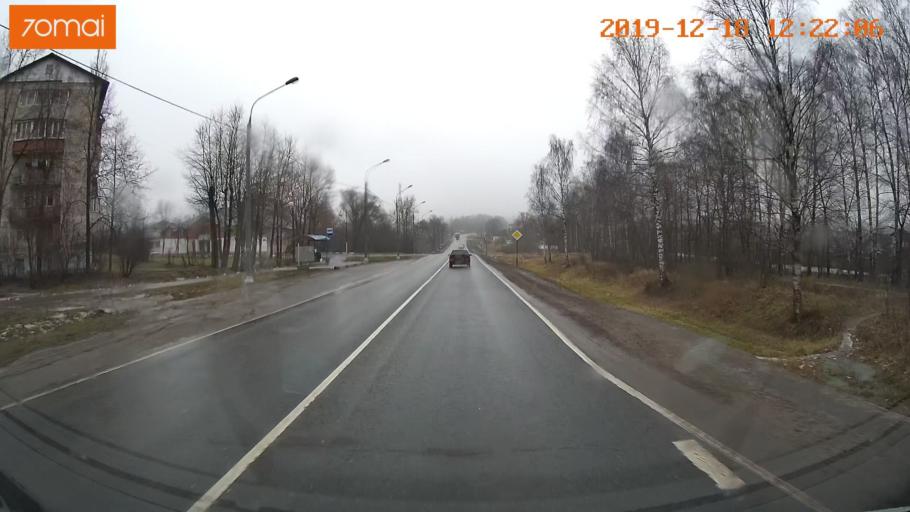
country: RU
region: Moskovskaya
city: Novopetrovskoye
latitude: 56.0031
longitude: 36.4782
